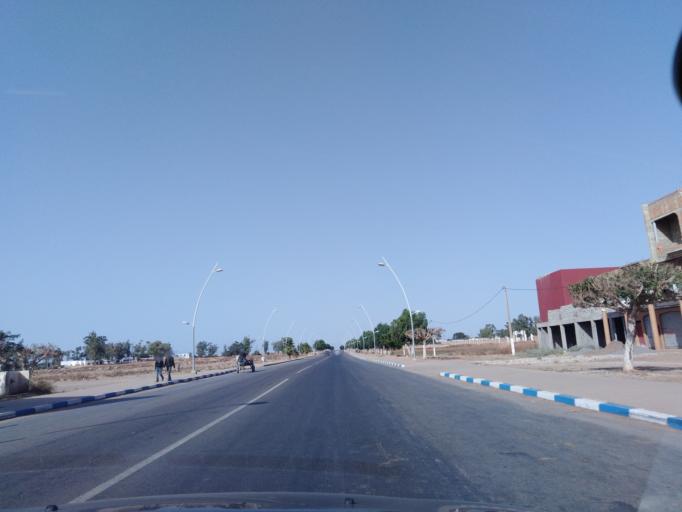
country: MA
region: Doukkala-Abda
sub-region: Safi
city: Safi
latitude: 32.2557
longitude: -8.9784
